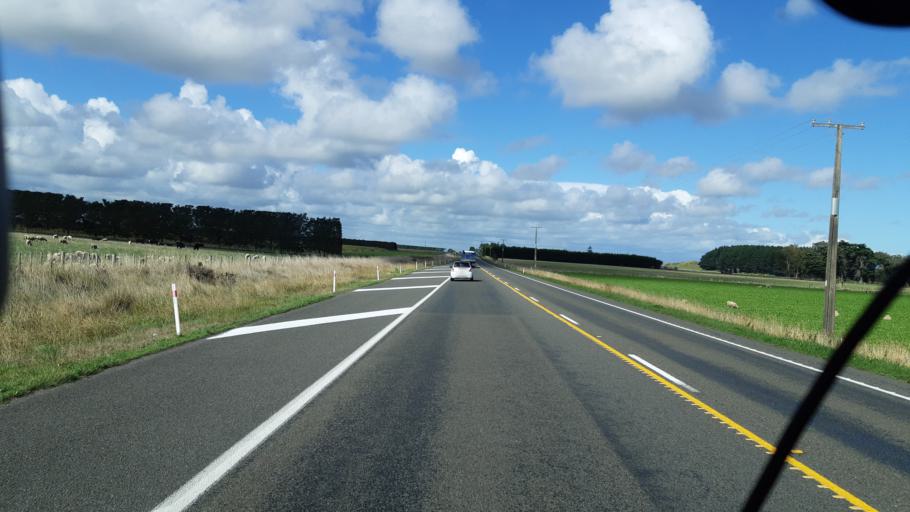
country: NZ
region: Manawatu-Wanganui
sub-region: Wanganui District
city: Wanganui
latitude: -39.9864
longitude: 175.1568
